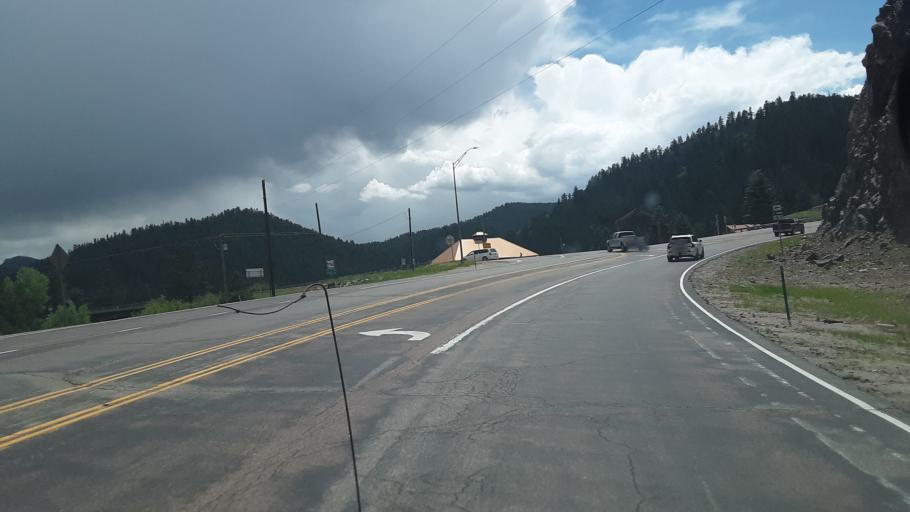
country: US
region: Colorado
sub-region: Fremont County
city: Florence
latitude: 38.1648
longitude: -105.1901
